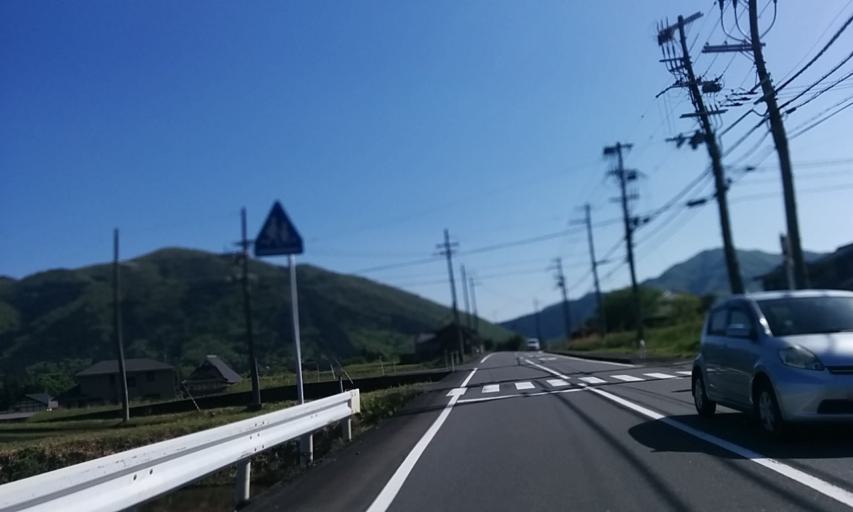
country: JP
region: Kyoto
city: Ayabe
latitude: 35.2534
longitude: 135.4226
